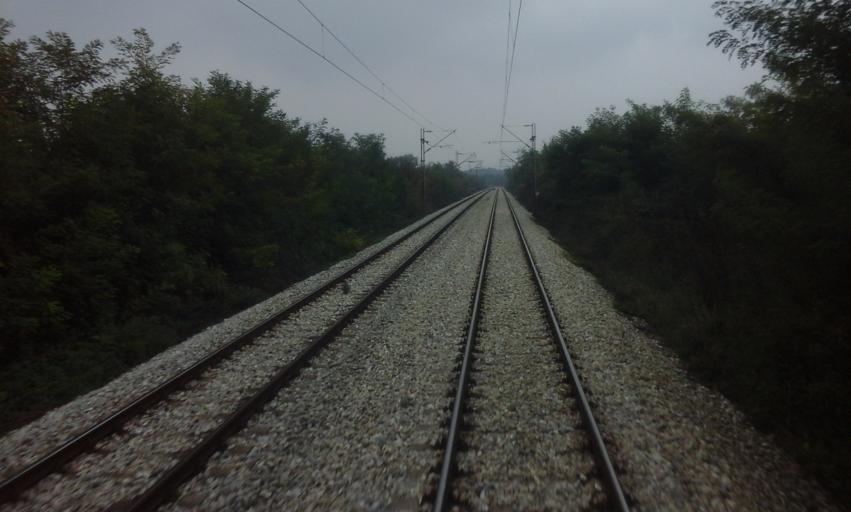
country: RS
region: Central Serbia
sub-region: Sumadijski Okrug
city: Lapovo
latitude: 44.2143
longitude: 21.0940
